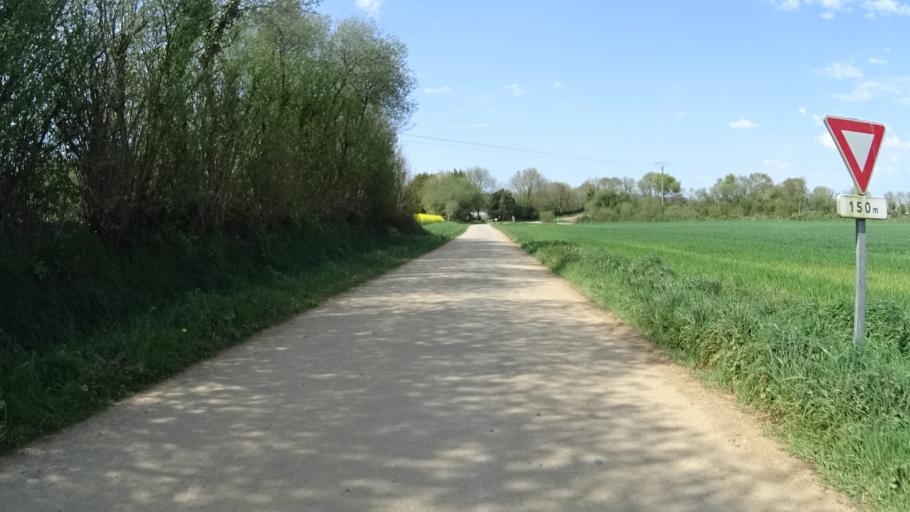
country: FR
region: Brittany
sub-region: Departement du Finistere
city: Sizun
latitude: 48.4259
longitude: -4.0906
